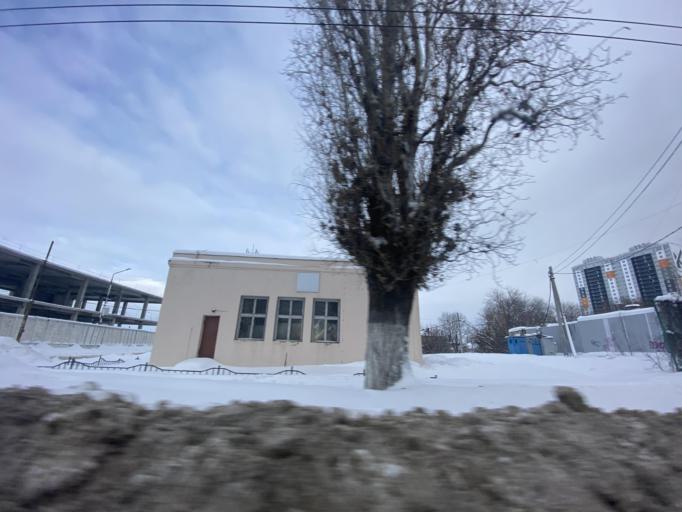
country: RU
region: Saratov
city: Engel's
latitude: 51.5004
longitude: 46.0846
